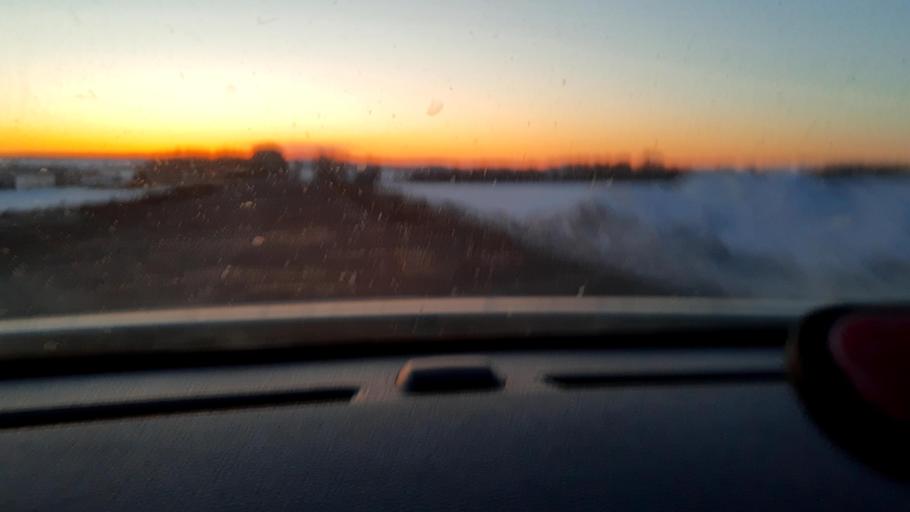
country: RU
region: Bashkortostan
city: Avdon
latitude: 54.3877
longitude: 55.7371
